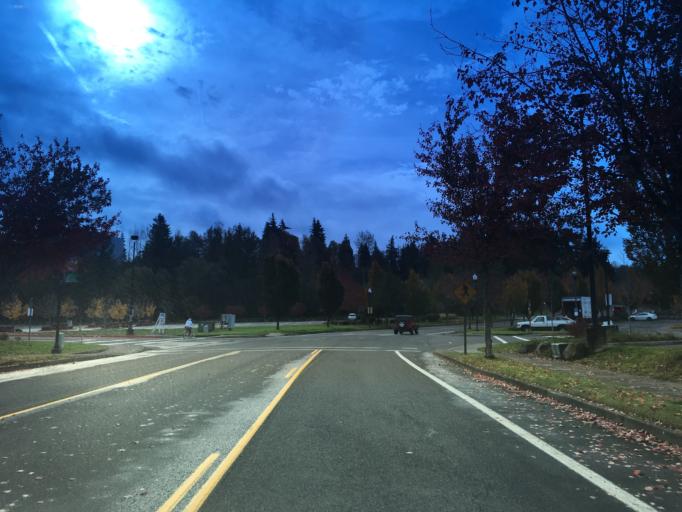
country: US
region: Oregon
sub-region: Multnomah County
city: Wood Village
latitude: 45.5303
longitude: -122.4272
